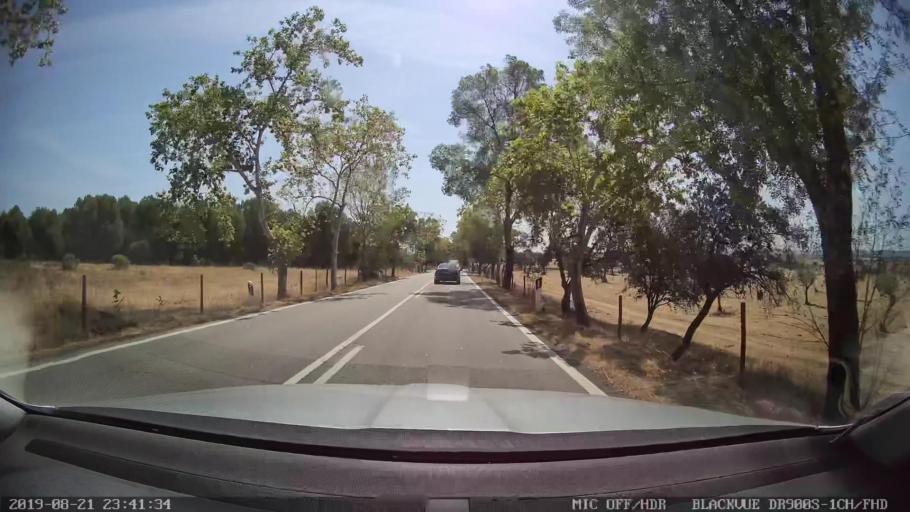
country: PT
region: Castelo Branco
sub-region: Idanha-A-Nova
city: Idanha-a-Nova
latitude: 39.8639
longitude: -7.3213
